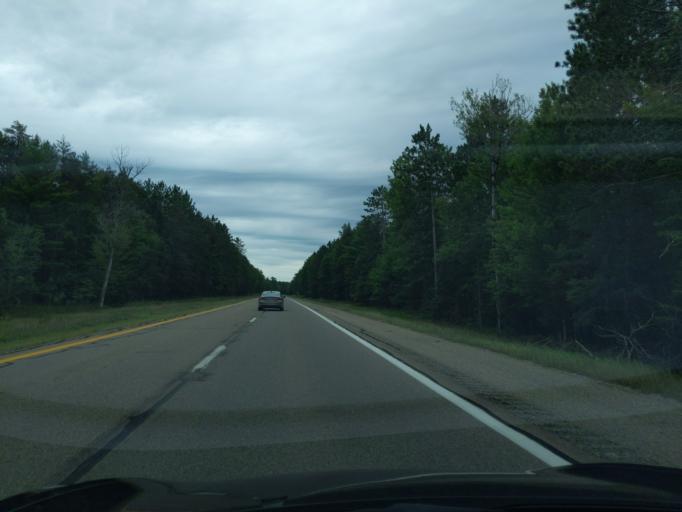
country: US
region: Michigan
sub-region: Roscommon County
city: Houghton Lake
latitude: 44.2337
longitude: -84.8021
